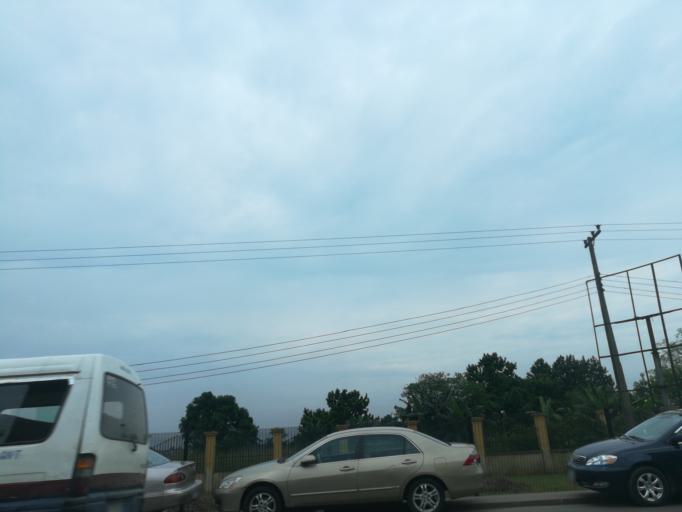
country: NG
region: Rivers
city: Port Harcourt
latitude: 4.8420
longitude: 6.9843
